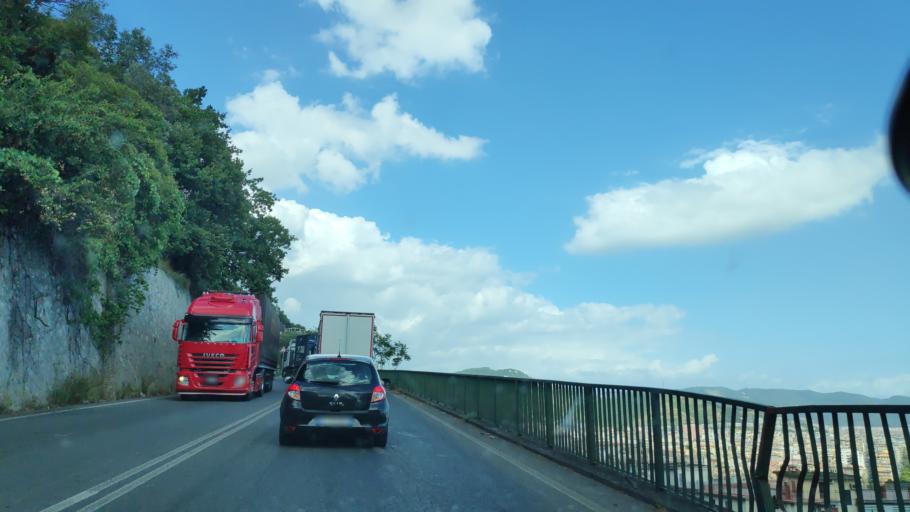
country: IT
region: Campania
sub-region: Provincia di Salerno
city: Vietri sul Mare
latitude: 40.6805
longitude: 14.7500
